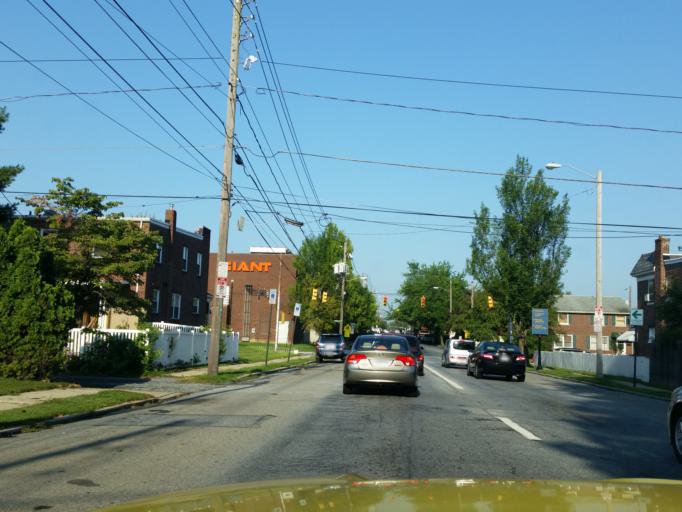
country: US
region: Pennsylvania
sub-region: Lancaster County
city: Lancaster
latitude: 40.0447
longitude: -76.2874
